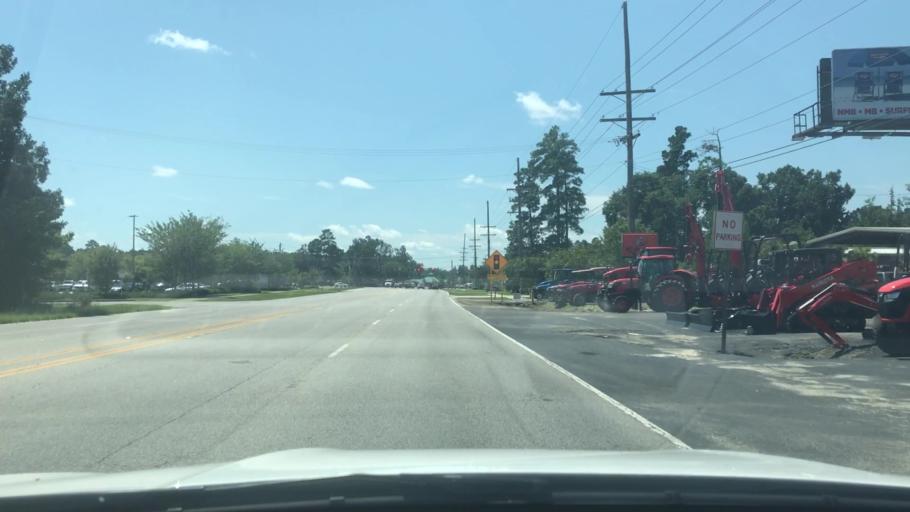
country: US
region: South Carolina
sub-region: Horry County
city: Conway
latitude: 33.8692
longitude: -79.0525
